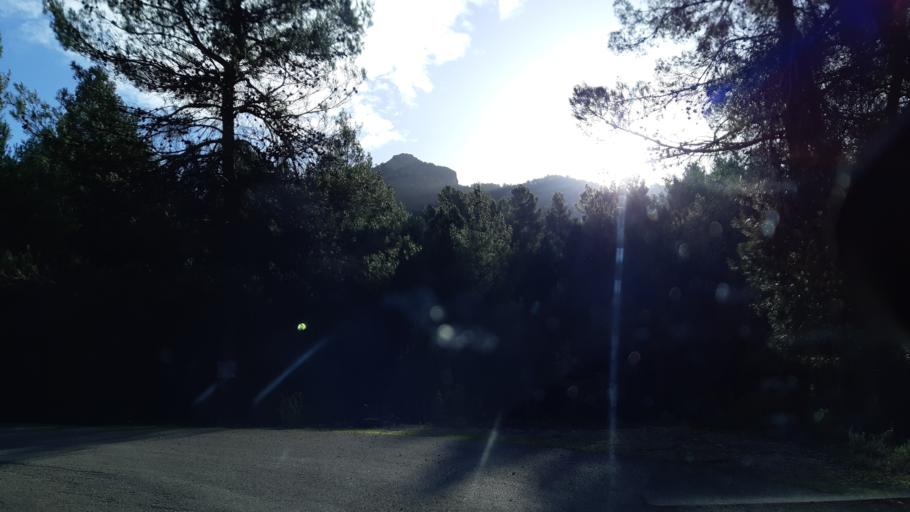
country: ES
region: Aragon
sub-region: Provincia de Teruel
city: Valderrobres
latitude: 40.8482
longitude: 0.2127
